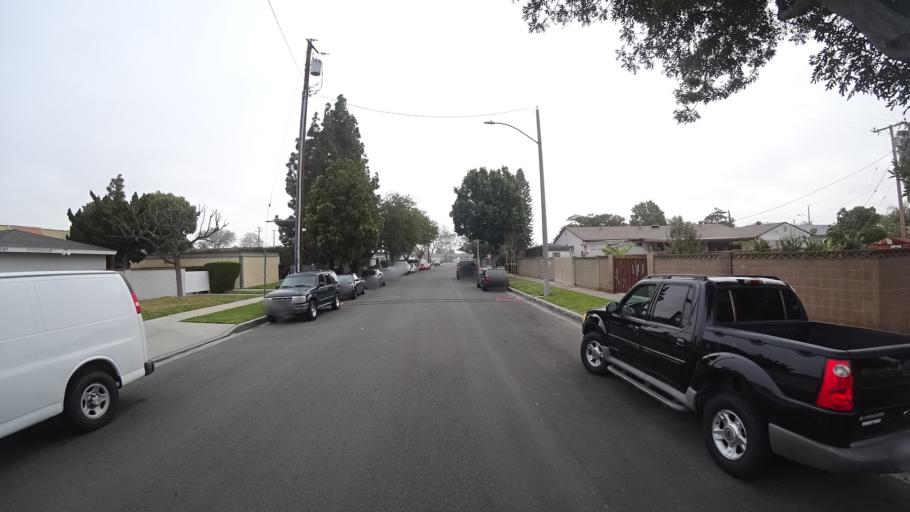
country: US
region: California
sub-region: Orange County
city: Stanton
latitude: 33.8156
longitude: -118.0009
